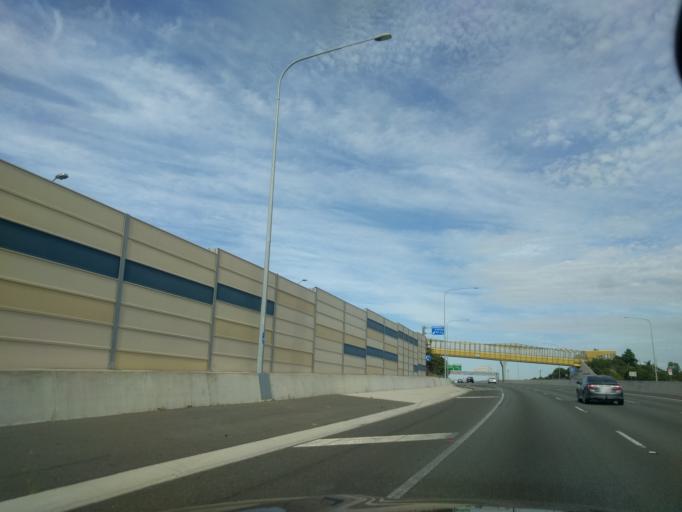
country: AU
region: Queensland
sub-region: Ipswich
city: Riverview
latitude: -27.5976
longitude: 152.8532
